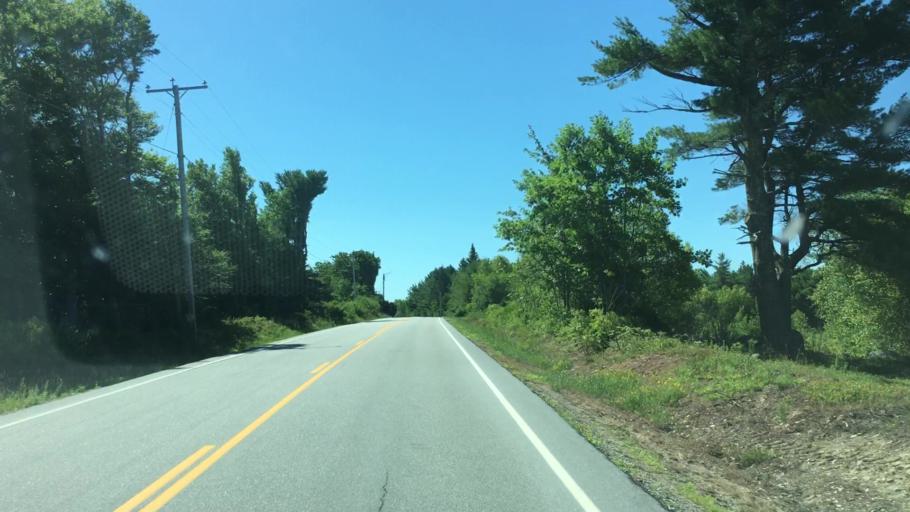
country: US
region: Maine
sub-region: Hancock County
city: Orland
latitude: 44.5477
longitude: -68.6896
